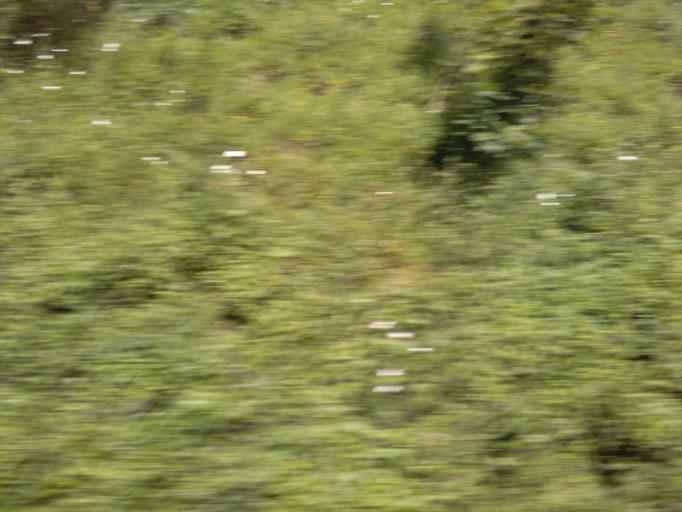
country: GB
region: England
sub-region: Hertfordshire
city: Harpenden
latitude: 51.8550
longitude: -0.3753
